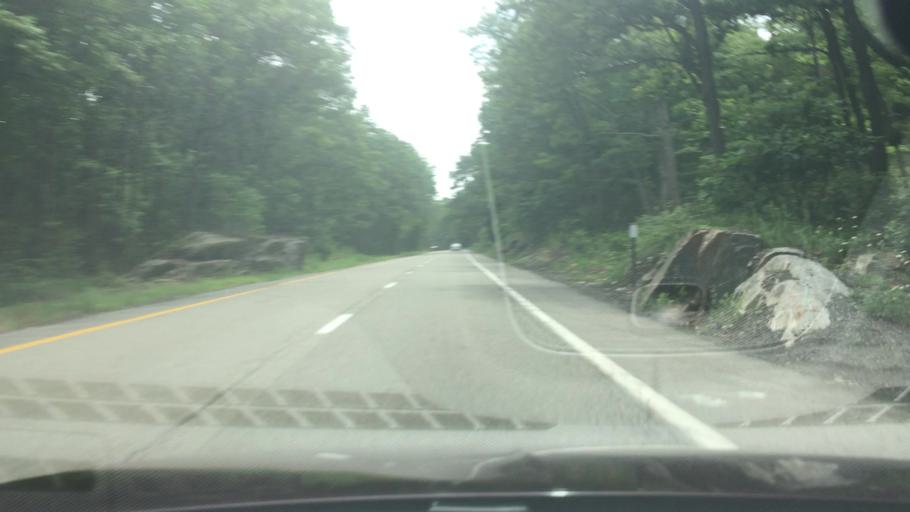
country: US
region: New York
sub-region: Dutchess County
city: Brinckerhoff
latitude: 41.4582
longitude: -73.8190
